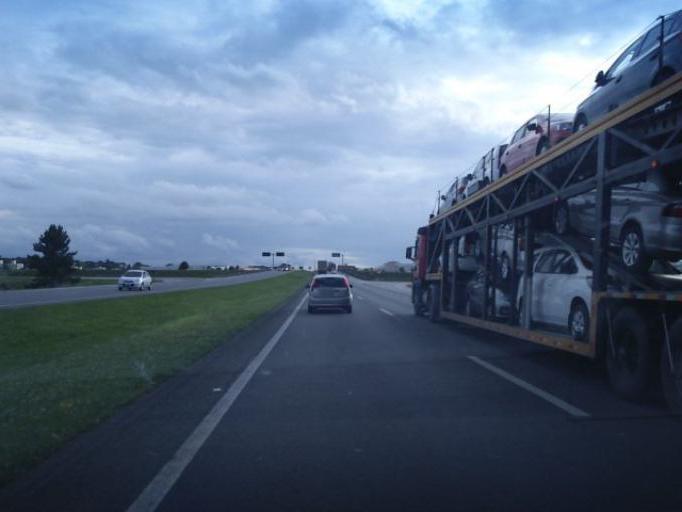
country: BR
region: Parana
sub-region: Sao Jose Dos Pinhais
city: Sao Jose dos Pinhais
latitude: -25.5080
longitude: -49.1255
